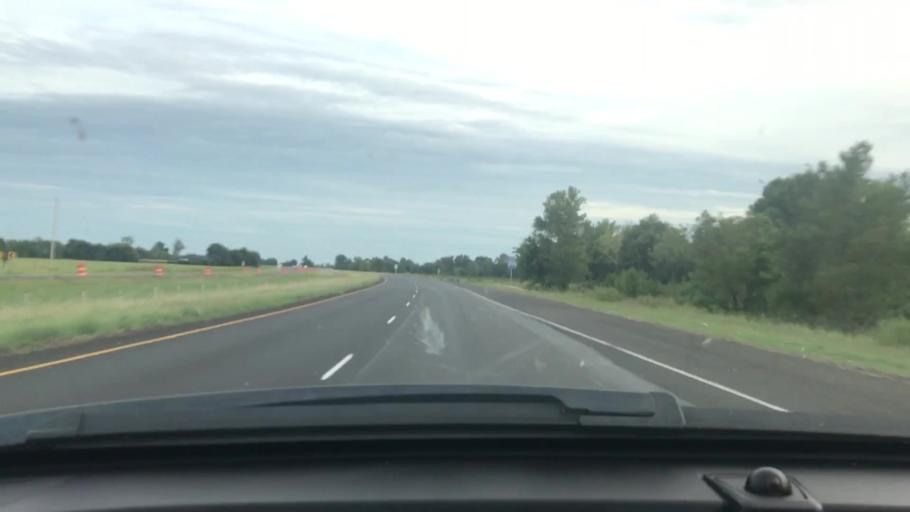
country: US
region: Arkansas
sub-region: Poinsett County
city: Trumann
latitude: 35.6724
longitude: -90.5530
